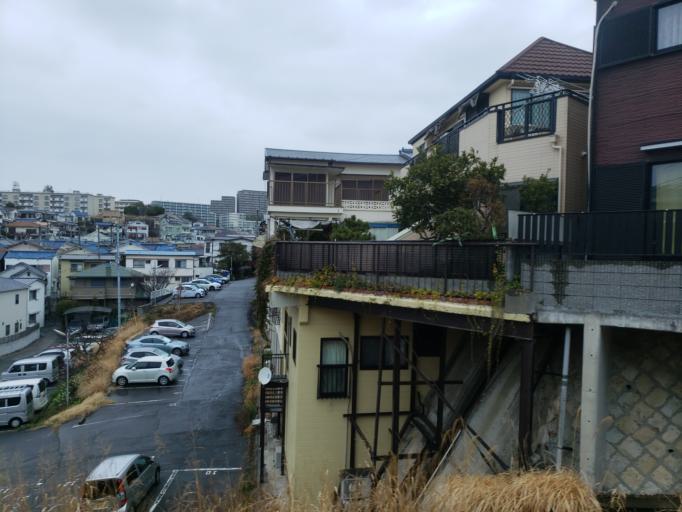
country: JP
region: Hyogo
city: Akashi
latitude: 34.6333
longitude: 135.0378
